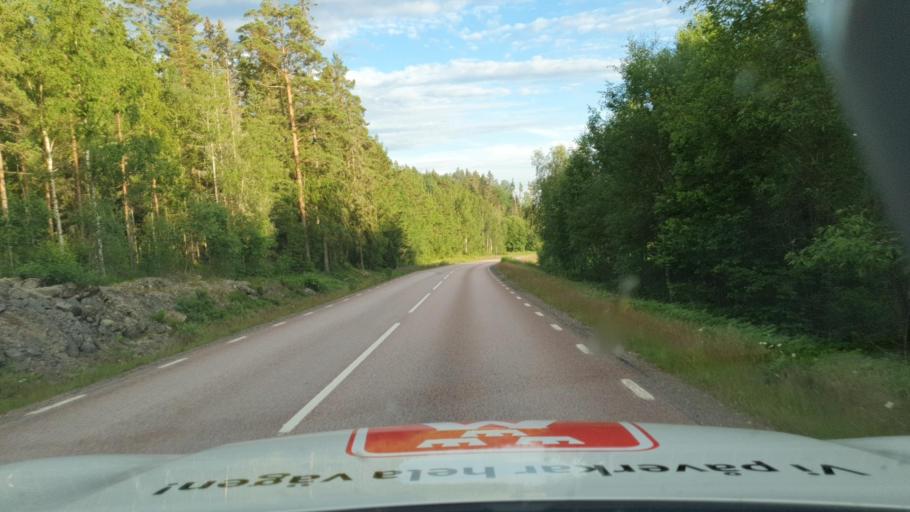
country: SE
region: Vaermland
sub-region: Karlstads Kommun
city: Molkom
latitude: 59.4931
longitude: 13.8033
